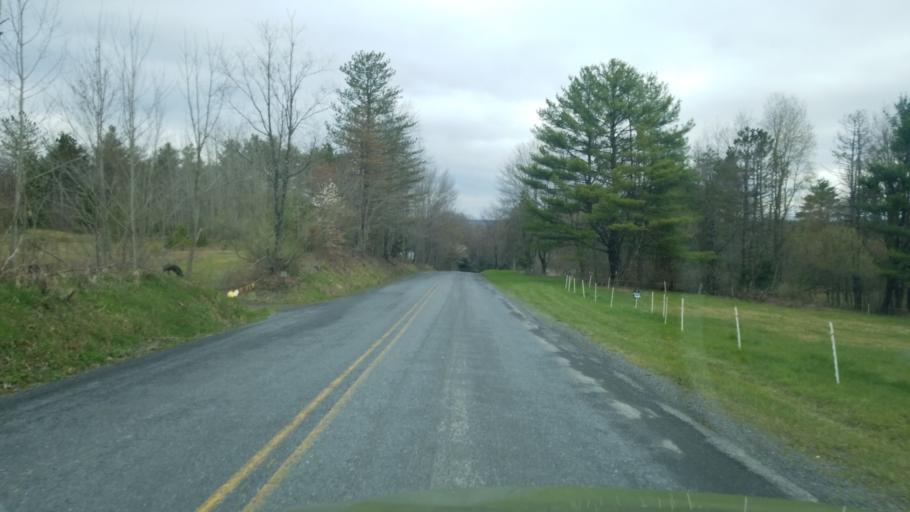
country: US
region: Pennsylvania
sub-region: Clearfield County
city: Clearfield
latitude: 41.0580
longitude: -78.4272
